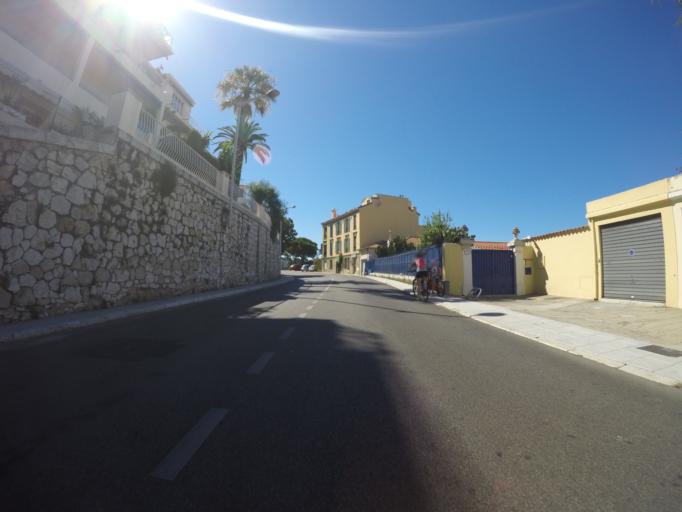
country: FR
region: Provence-Alpes-Cote d'Azur
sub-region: Departement des Alpes-Maritimes
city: Villefranche-sur-Mer
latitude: 43.6929
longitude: 7.2932
